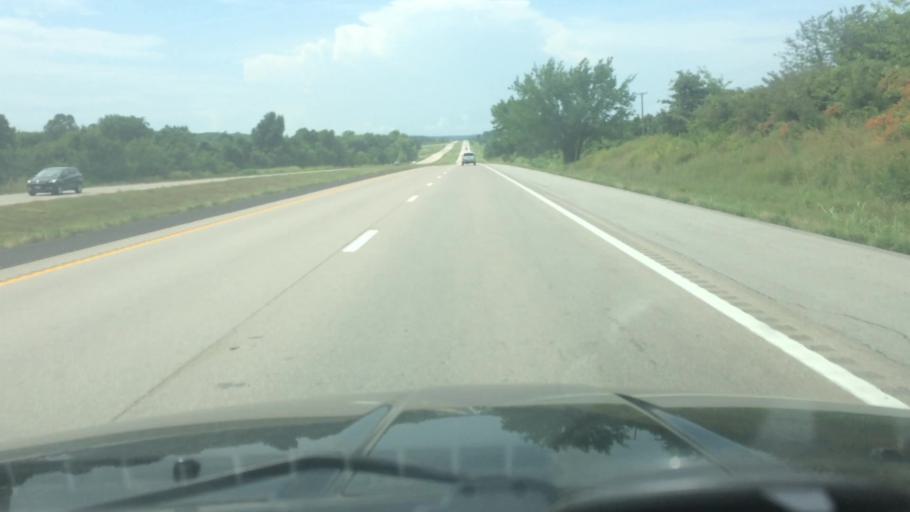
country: US
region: Missouri
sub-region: Polk County
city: Humansville
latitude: 37.7821
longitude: -93.5766
